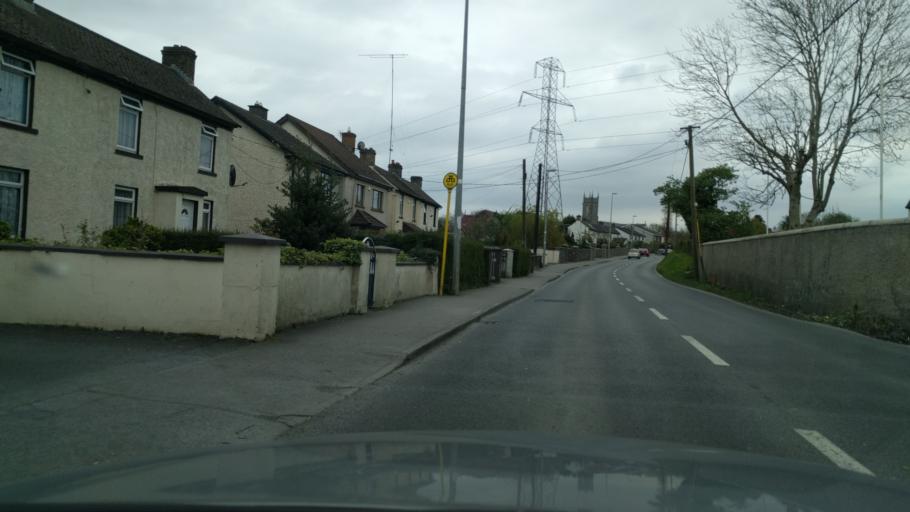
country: IE
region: Leinster
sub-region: South Dublin
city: Saggart
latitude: 53.2817
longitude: -6.4478
